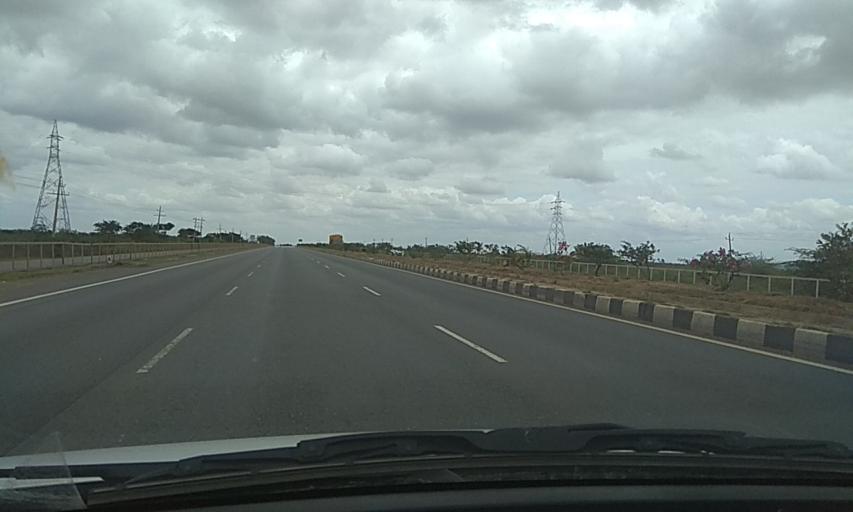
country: IN
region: Karnataka
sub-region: Chitradurga
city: Hiriyur
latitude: 13.8654
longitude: 76.7085
